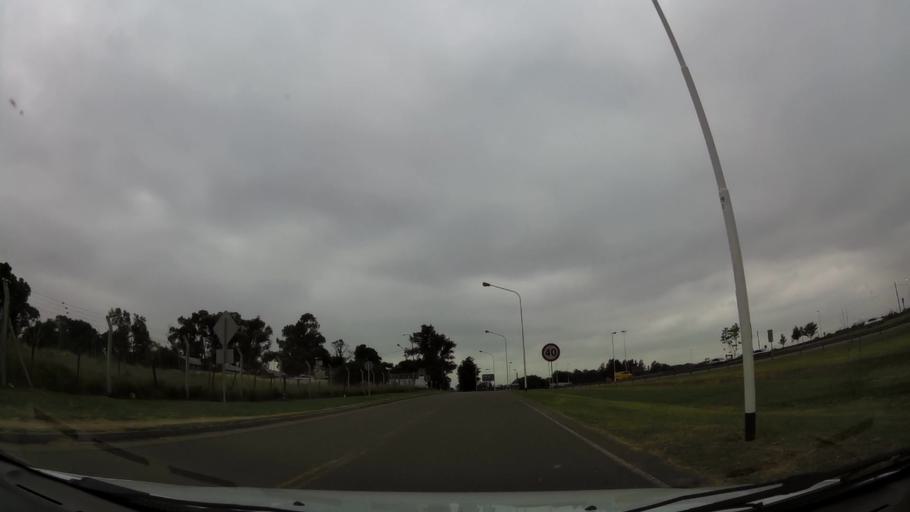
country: AR
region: Buenos Aires F.D.
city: Villa Lugano
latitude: -34.7259
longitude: -58.5163
